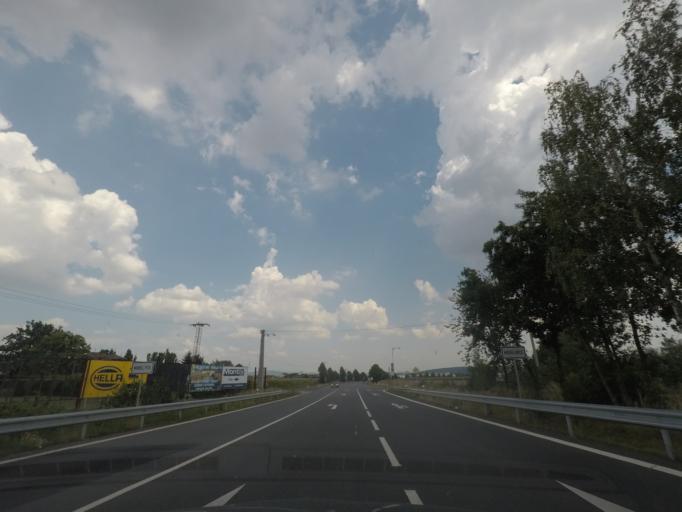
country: CZ
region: Olomoucky
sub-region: Okres Sumperk
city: Mohelnice
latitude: 49.7684
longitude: 16.9183
